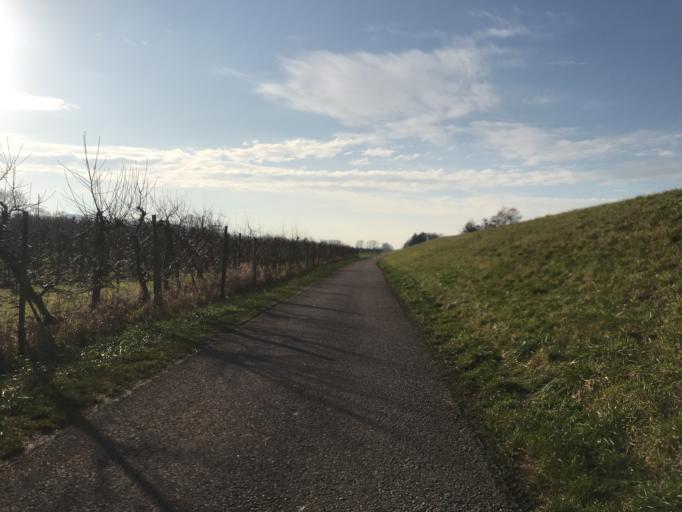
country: DE
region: Hesse
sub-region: Regierungsbezirk Darmstadt
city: Eltville
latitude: 50.0121
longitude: 8.1306
